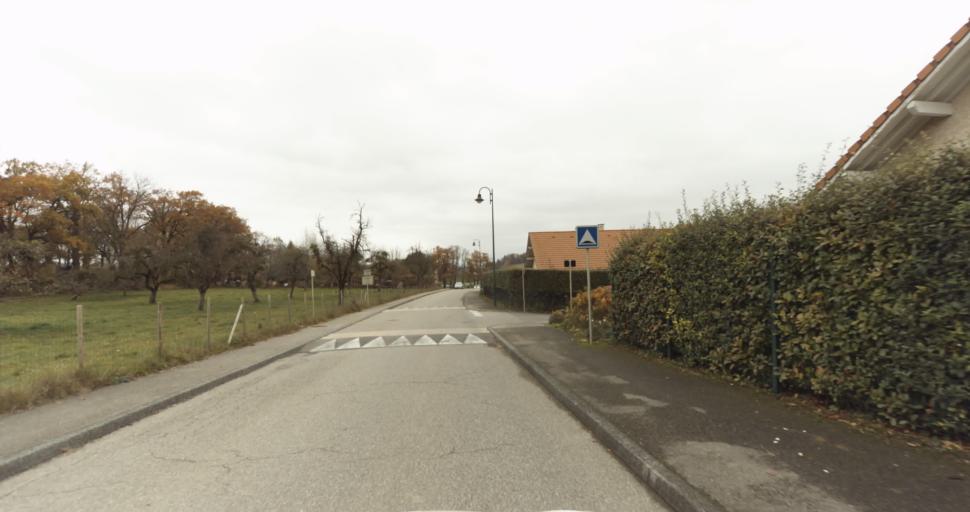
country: FR
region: Rhone-Alpes
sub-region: Departement de la Haute-Savoie
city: Chavanod
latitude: 45.8615
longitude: 6.0537
